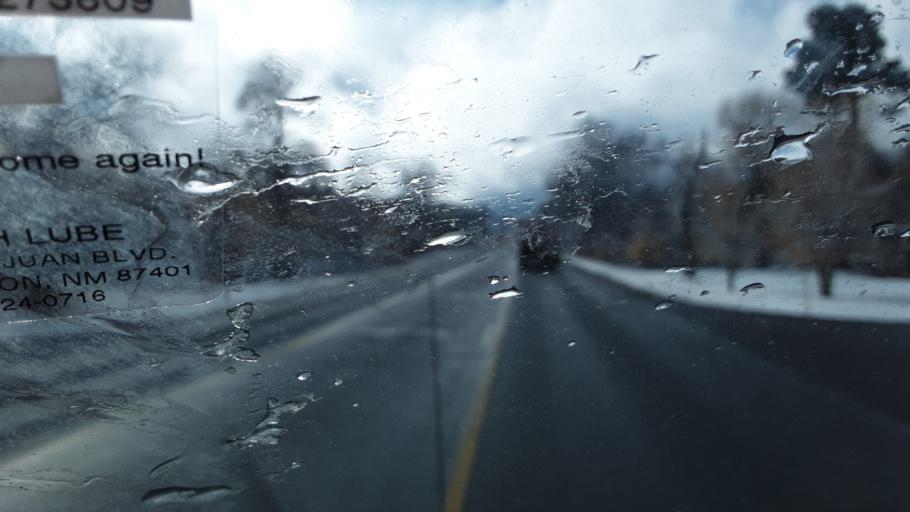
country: US
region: Colorado
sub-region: La Plata County
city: Bayfield
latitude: 37.2302
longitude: -107.6036
